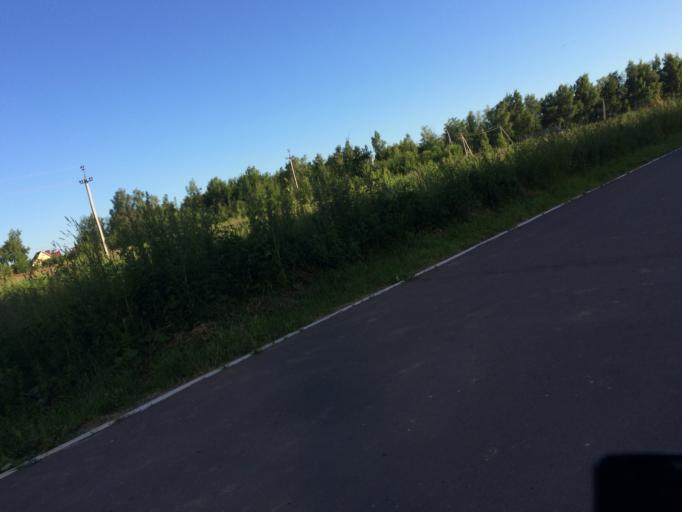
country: RU
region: Mariy-El
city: Medvedevo
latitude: 56.6487
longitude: 47.8338
